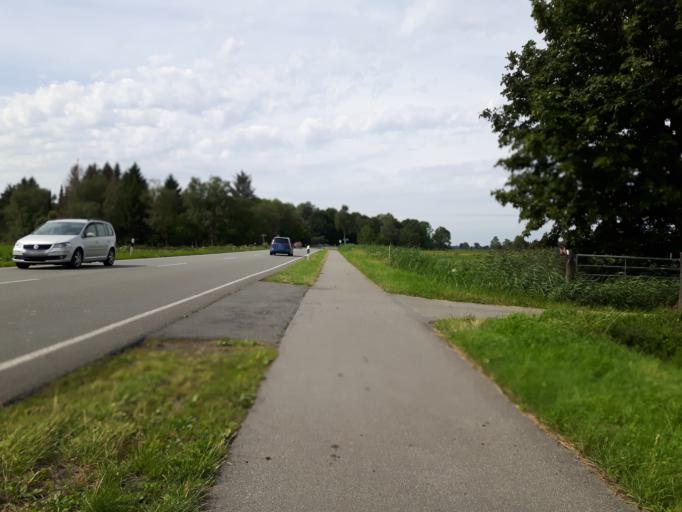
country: DE
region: Lower Saxony
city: Ovelgonne
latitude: 53.2699
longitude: 8.3529
